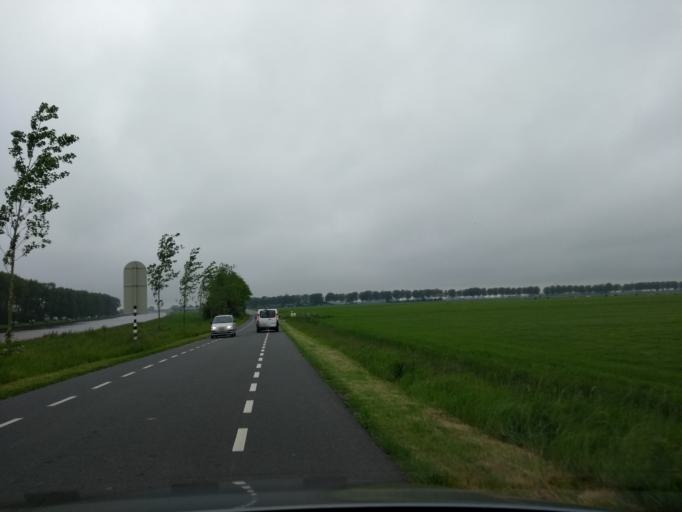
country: NL
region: Groningen
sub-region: Gemeente Zuidhorn
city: Aduard
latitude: 53.2594
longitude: 6.5011
